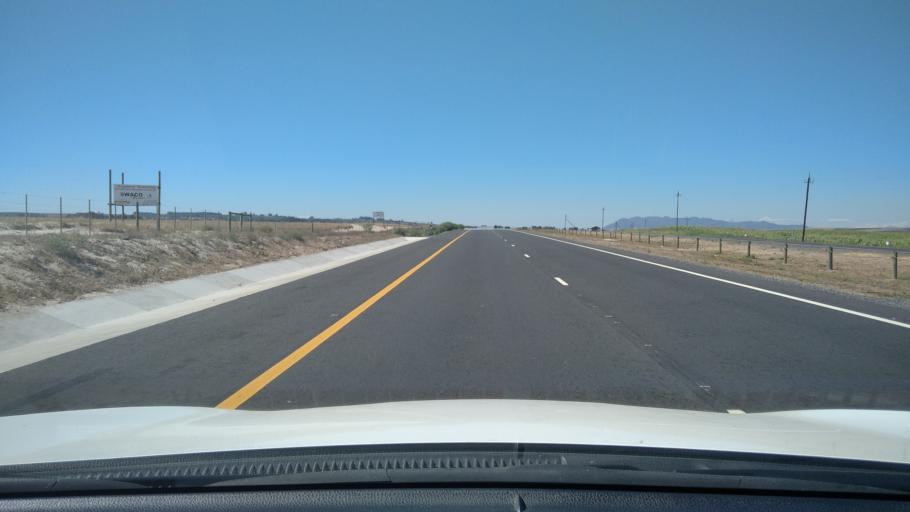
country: ZA
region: Western Cape
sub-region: West Coast District Municipality
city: Malmesbury
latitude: -33.5536
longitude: 18.6303
